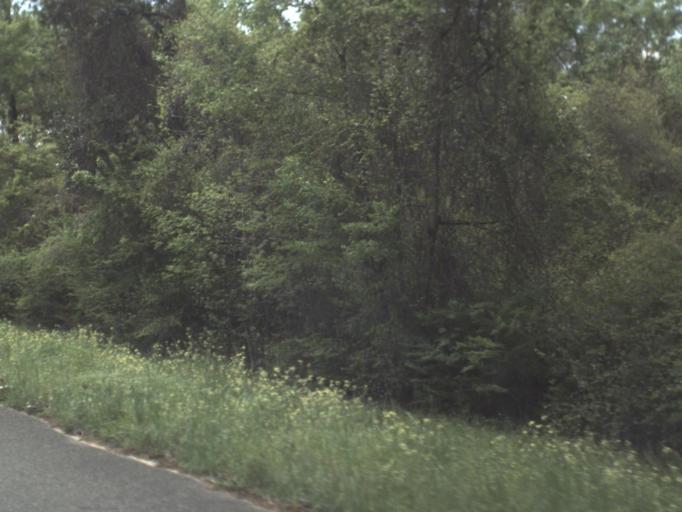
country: US
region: Florida
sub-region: Okaloosa County
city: Crestview
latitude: 30.9217
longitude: -86.6373
